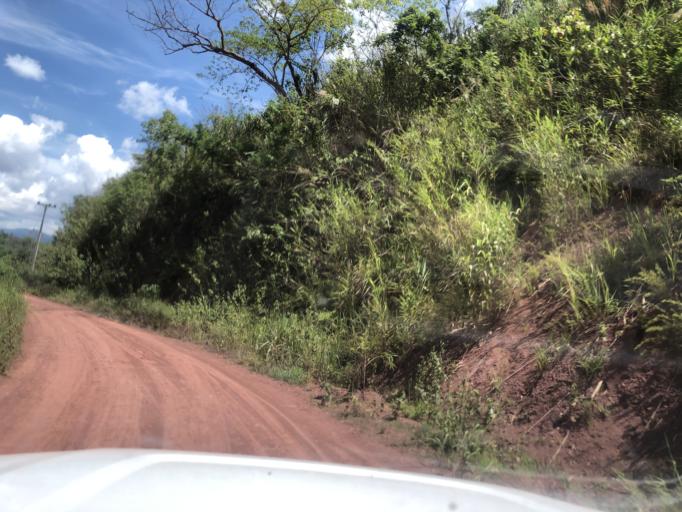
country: CN
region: Yunnan
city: Menglie
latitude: 22.2434
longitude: 101.6095
